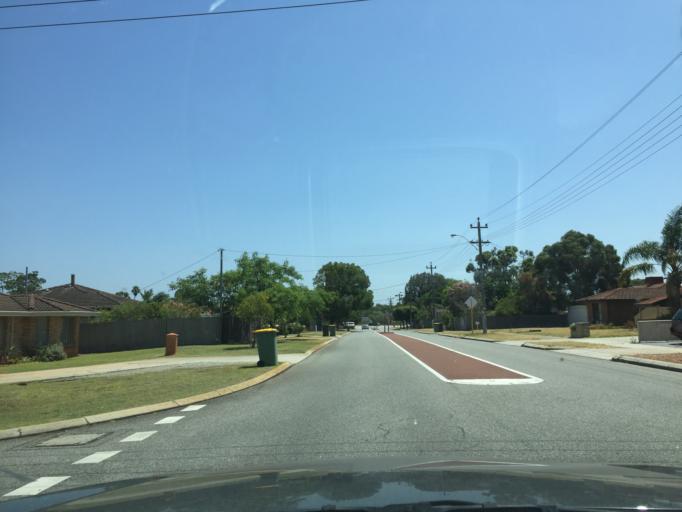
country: AU
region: Western Australia
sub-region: Canning
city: Ferndale
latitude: -32.0403
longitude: 115.9141
